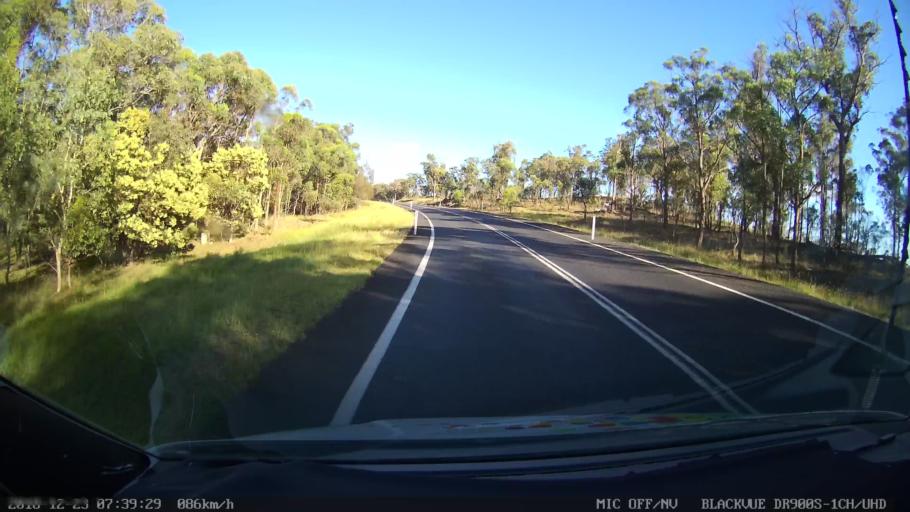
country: AU
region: New South Wales
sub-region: Armidale Dumaresq
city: Enmore
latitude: -30.5162
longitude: 152.0203
